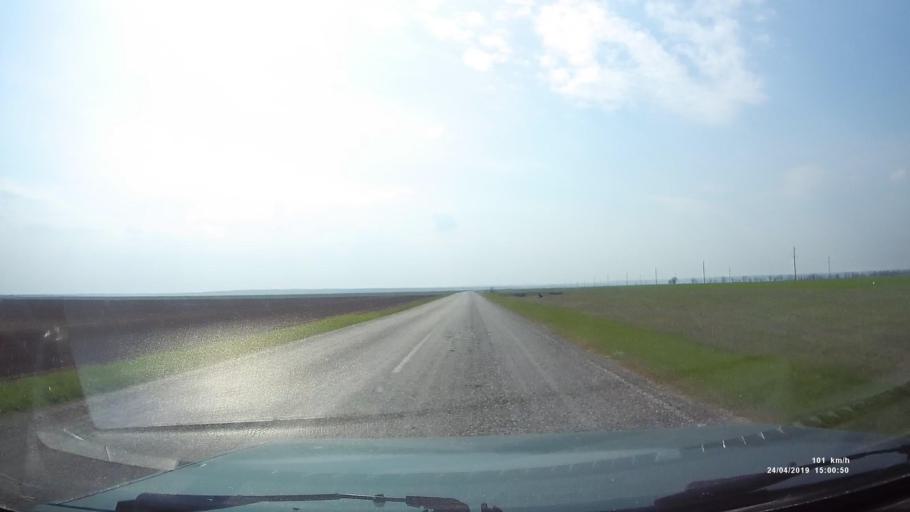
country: RU
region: Rostov
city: Remontnoye
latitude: 46.5654
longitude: 43.5469
